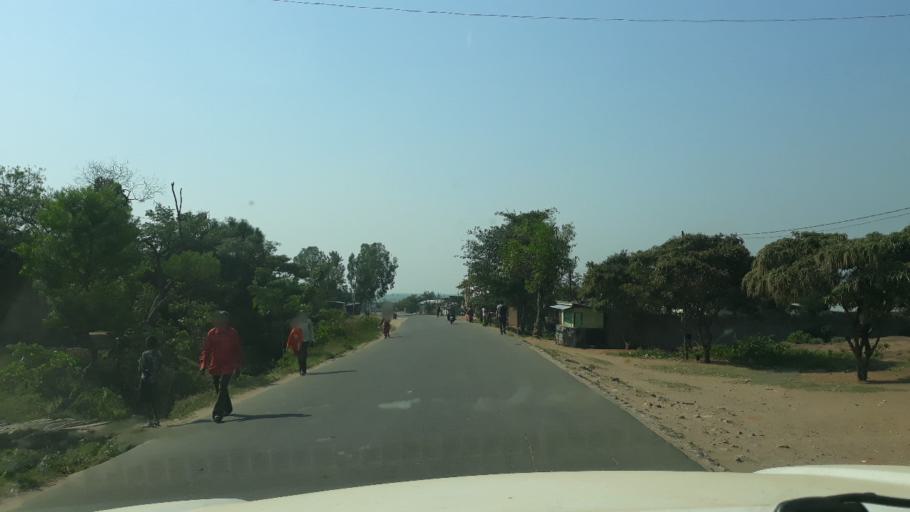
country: CD
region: South Kivu
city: Uvira
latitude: -3.2320
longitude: 29.1658
